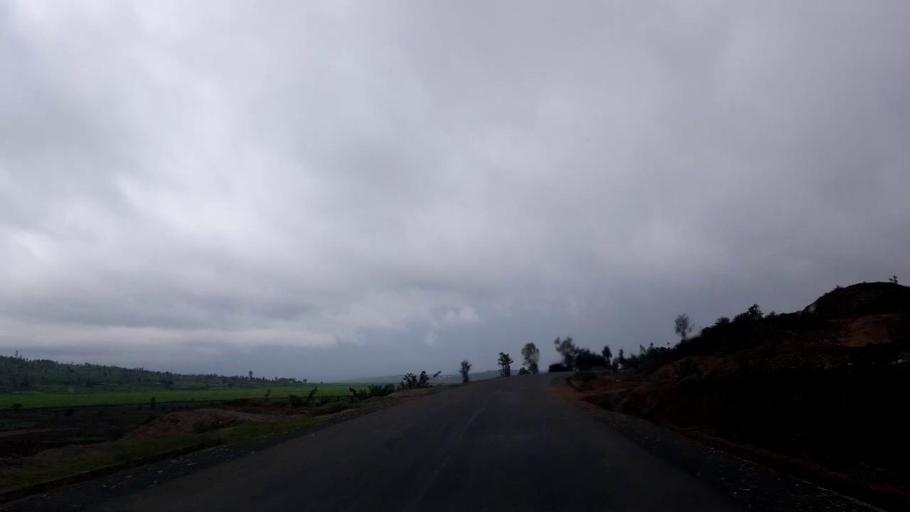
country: RW
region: Northern Province
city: Byumba
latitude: -1.4254
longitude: 30.2672
